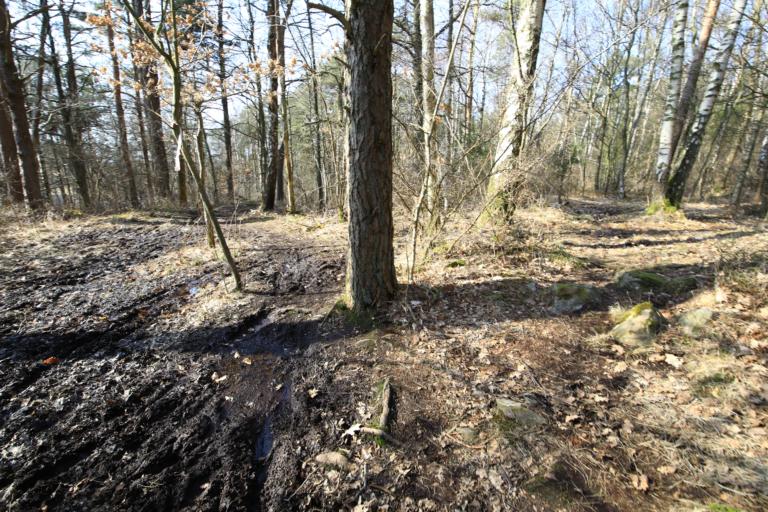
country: SE
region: Halland
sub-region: Varbergs Kommun
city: Varberg
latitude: 57.1453
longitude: 12.2840
